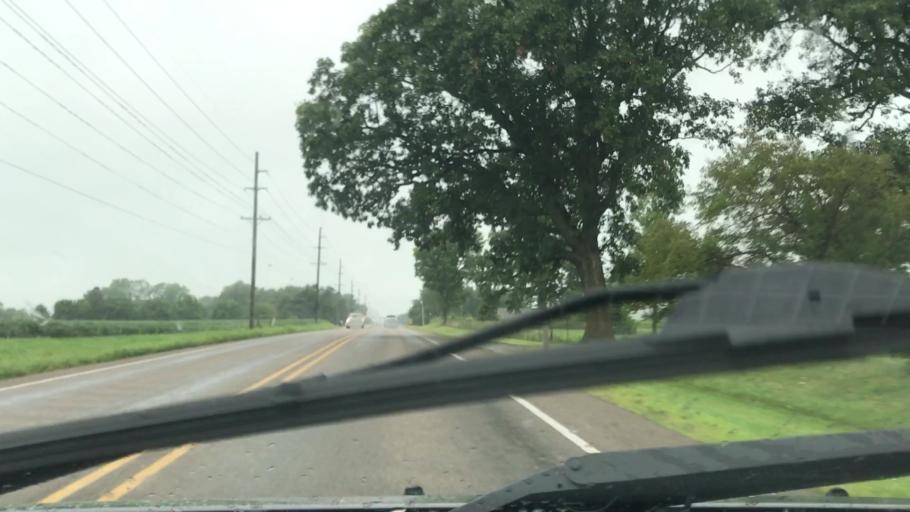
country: US
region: Indiana
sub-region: Hamilton County
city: Westfield
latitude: 40.1034
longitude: -86.1491
